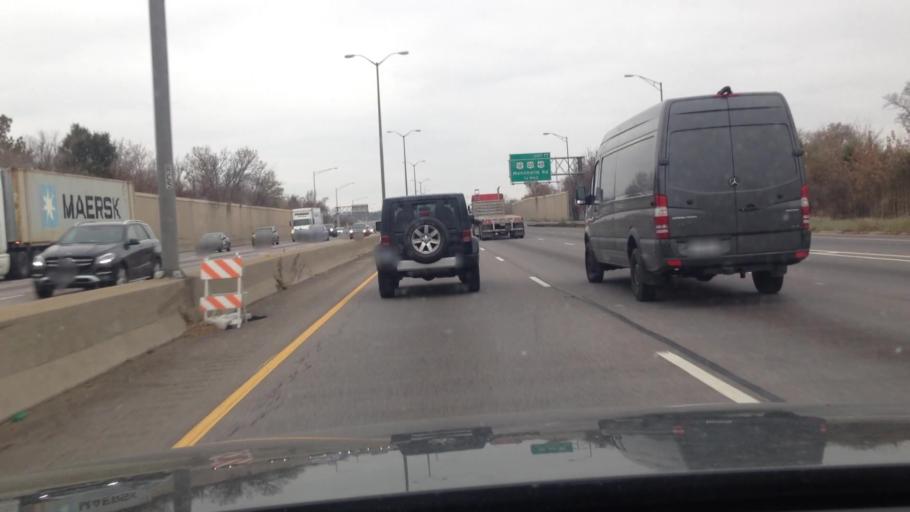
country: US
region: Illinois
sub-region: Cook County
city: Bellwood
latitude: 41.8709
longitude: -87.8701
